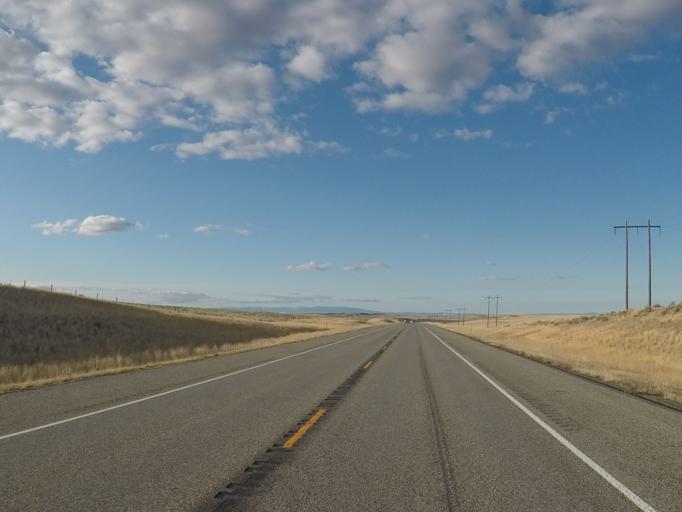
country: US
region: Montana
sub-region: Golden Valley County
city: Ryegate
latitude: 46.1756
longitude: -108.9080
